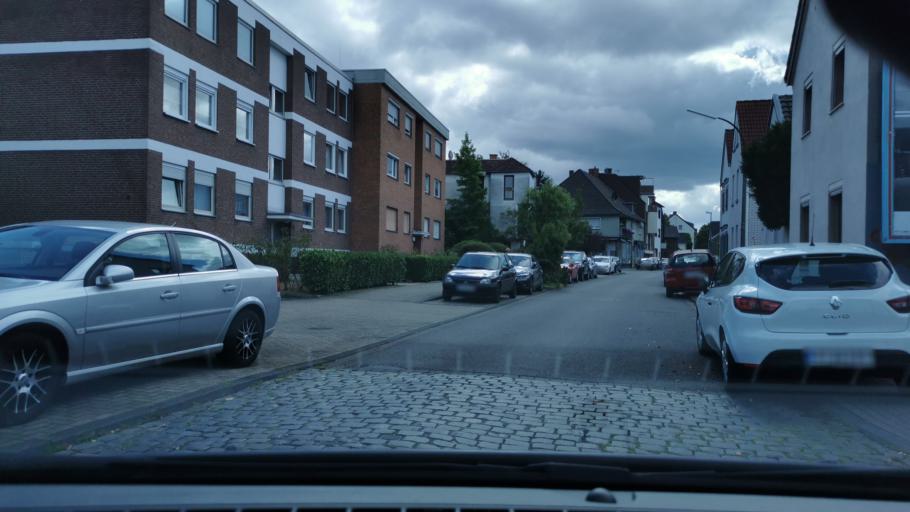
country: DE
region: North Rhine-Westphalia
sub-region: Regierungsbezirk Koln
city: Porz am Rhein
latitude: 50.8758
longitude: 7.0298
